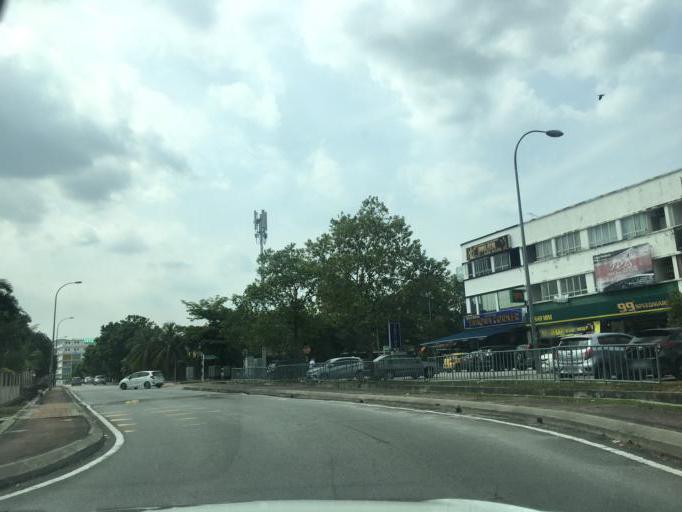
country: MY
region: Selangor
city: Shah Alam
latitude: 3.0758
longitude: 101.4887
